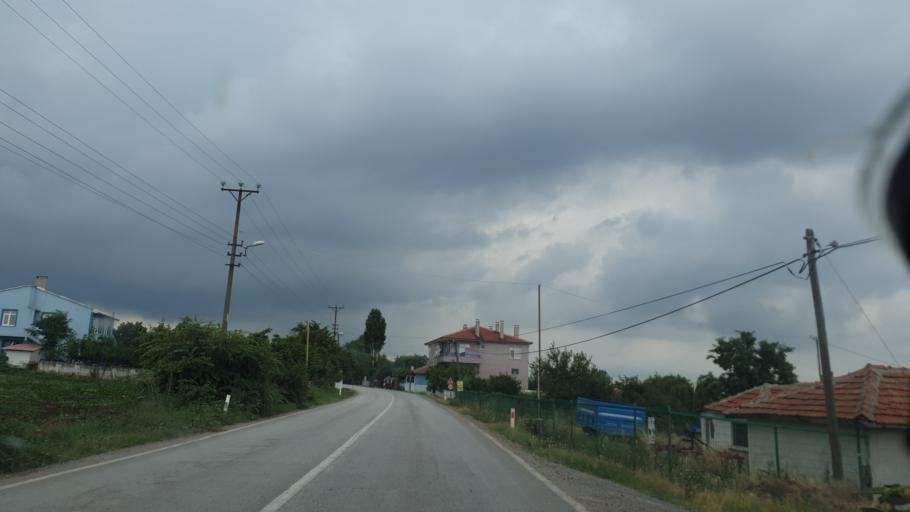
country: TR
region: Tekirdag
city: Hayrabolu
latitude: 41.2200
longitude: 26.9849
